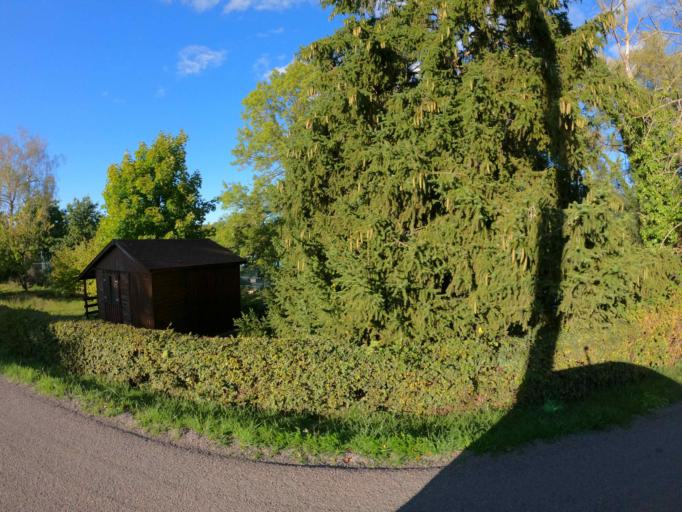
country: FR
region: Bourgogne
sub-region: Departement de Saone-et-Loire
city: Saint-Leu
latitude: 46.7547
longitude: 4.5068
